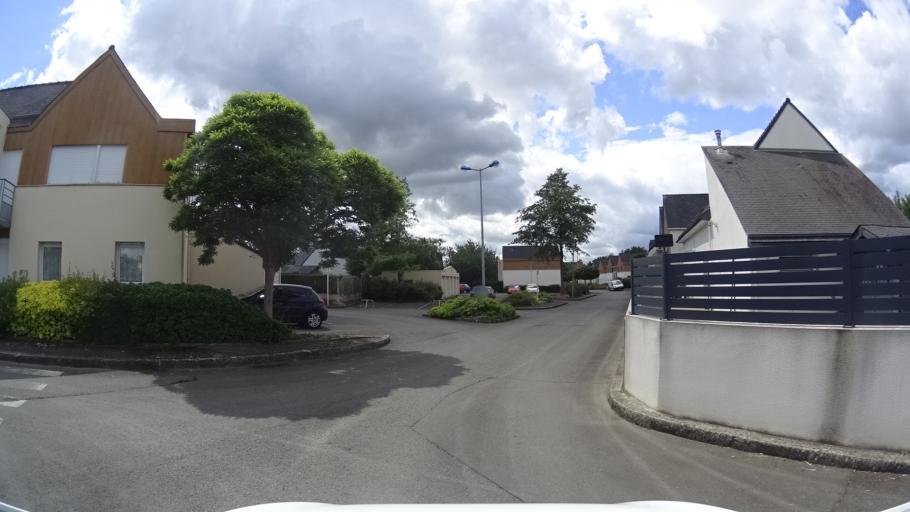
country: FR
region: Brittany
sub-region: Departement d'Ille-et-Vilaine
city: Chartres-de-Bretagne
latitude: 48.0348
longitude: -1.7136
